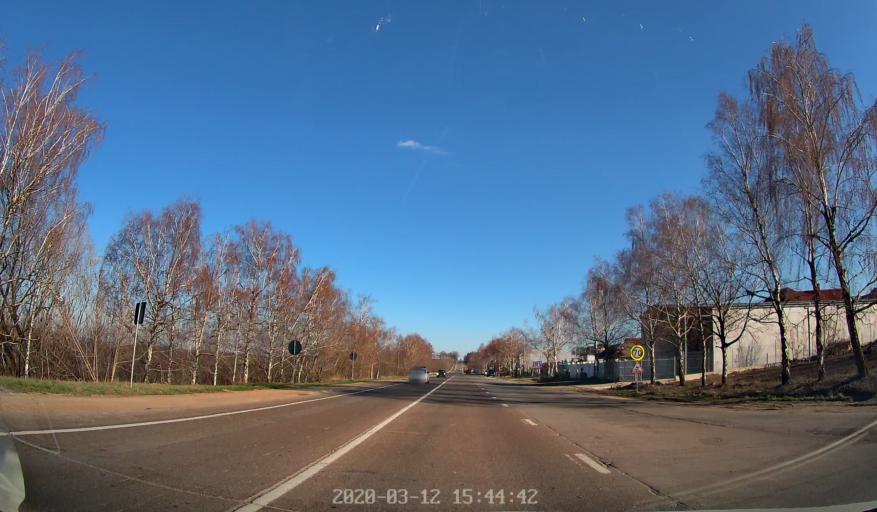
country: MD
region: Chisinau
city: Stauceni
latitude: 47.1097
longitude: 28.8649
